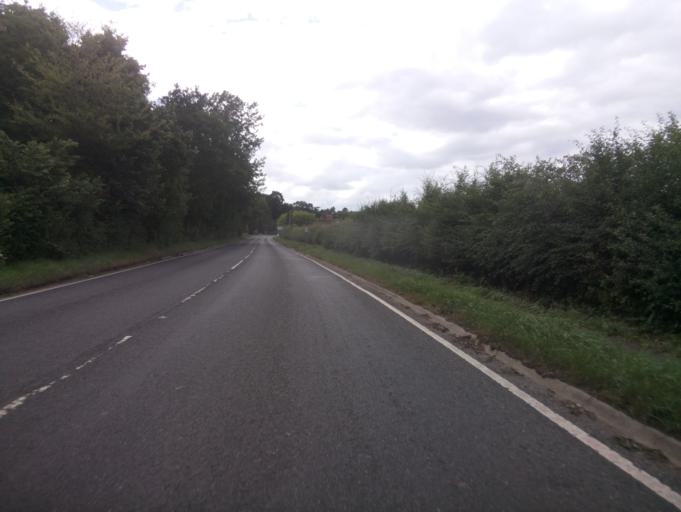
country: GB
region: England
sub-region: Warwickshire
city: Nuneaton
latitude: 52.5518
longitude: -1.4776
